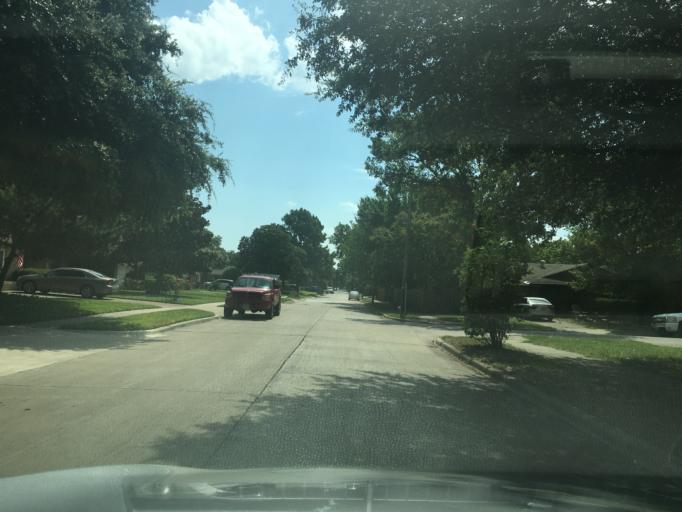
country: US
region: Texas
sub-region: Dallas County
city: Farmers Branch
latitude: 32.9312
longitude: -96.8713
